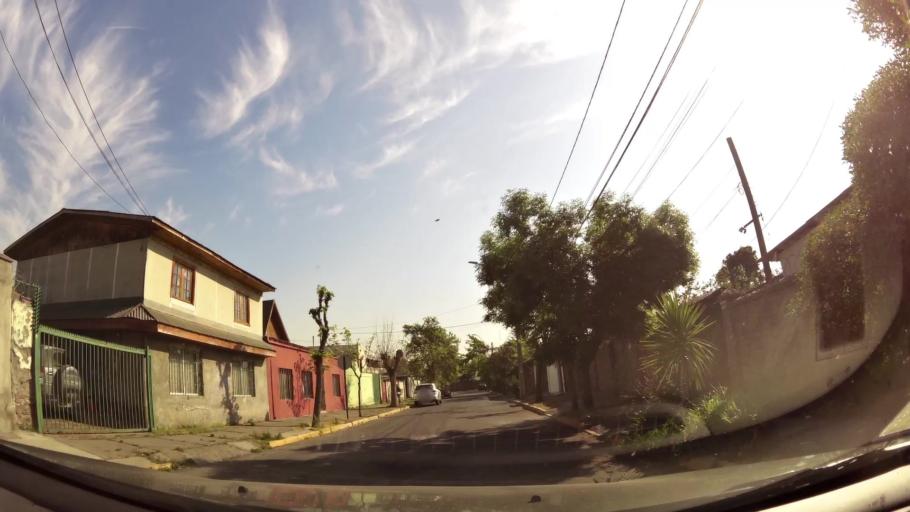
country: CL
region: Santiago Metropolitan
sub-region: Provincia de Maipo
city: San Bernardo
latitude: -33.5971
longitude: -70.7141
